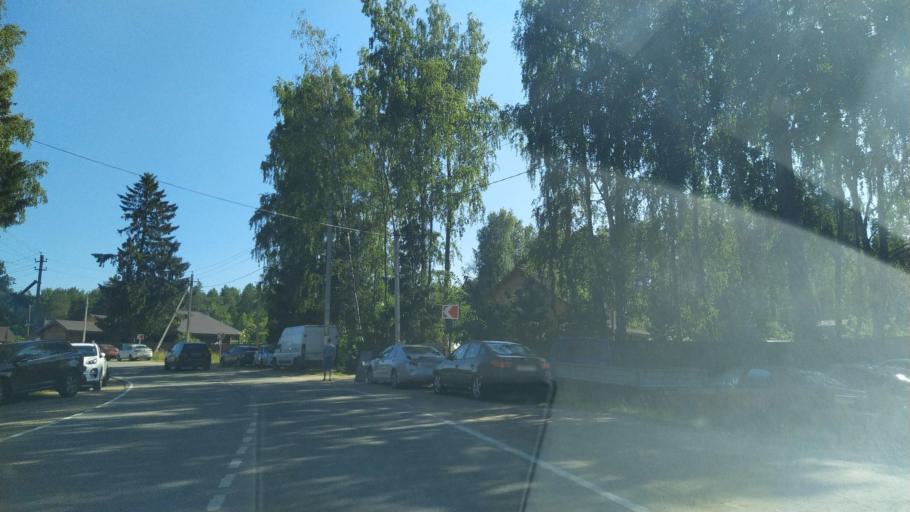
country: RU
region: Leningrad
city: Borisova Griva
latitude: 60.1209
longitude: 31.0740
